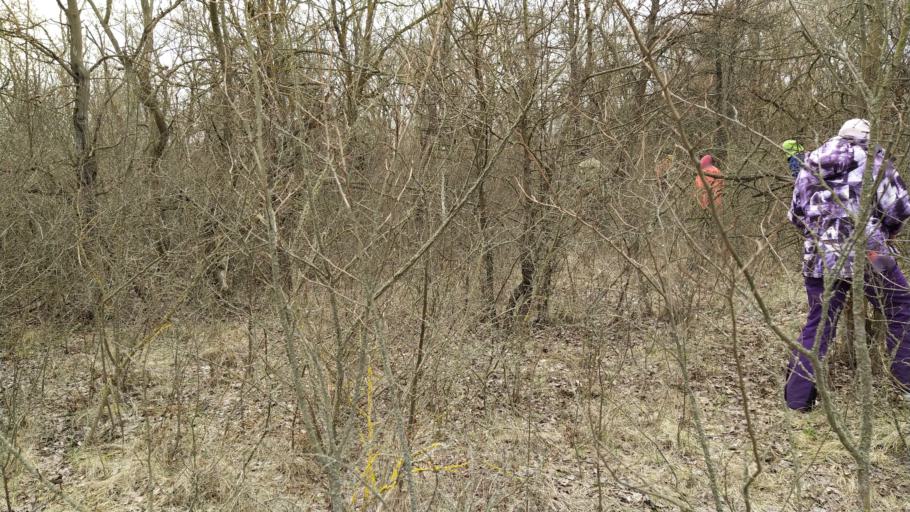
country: RU
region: Rostov
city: Semikarakorsk
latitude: 47.5393
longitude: 40.6813
